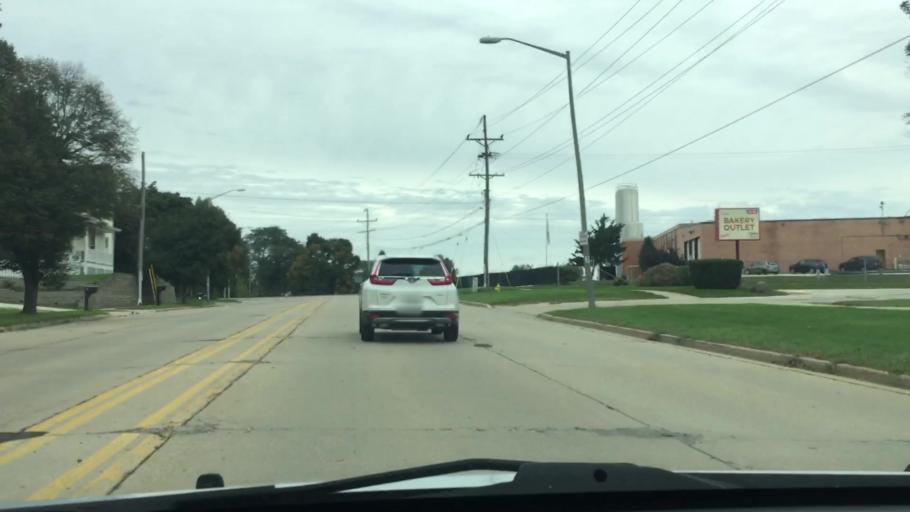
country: US
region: Wisconsin
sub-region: Waukesha County
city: Waukesha
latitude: 43.0298
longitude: -88.2431
